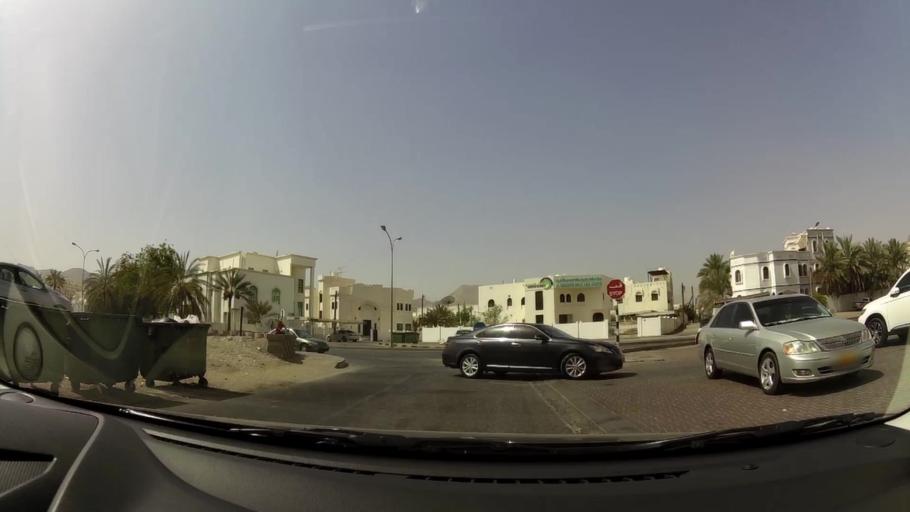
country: OM
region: Muhafazat Masqat
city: Bawshar
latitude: 23.5934
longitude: 58.4240
